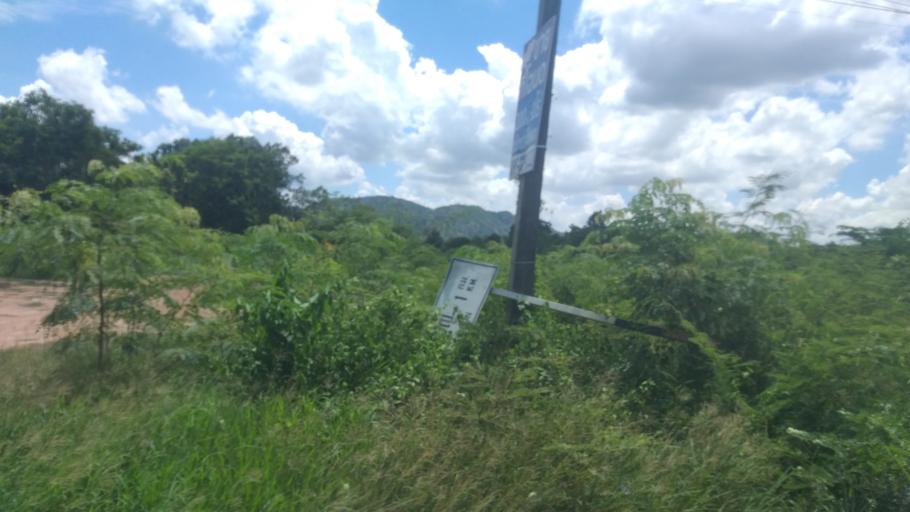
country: TH
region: Sara Buri
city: Wihan Daeng
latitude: 14.3981
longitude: 101.0988
